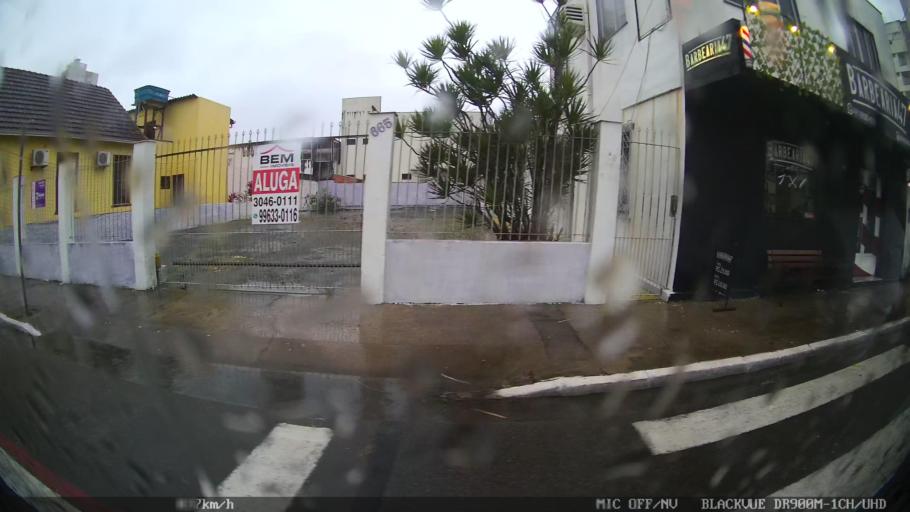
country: BR
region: Santa Catarina
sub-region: Itajai
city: Itajai
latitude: -26.9090
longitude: -48.6700
